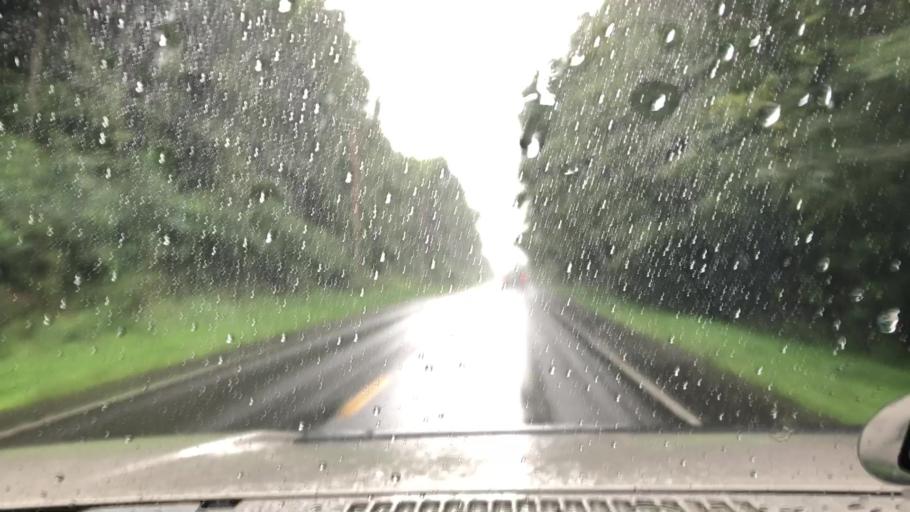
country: US
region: New York
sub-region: Greene County
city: Cairo
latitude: 42.2478
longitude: -73.9783
